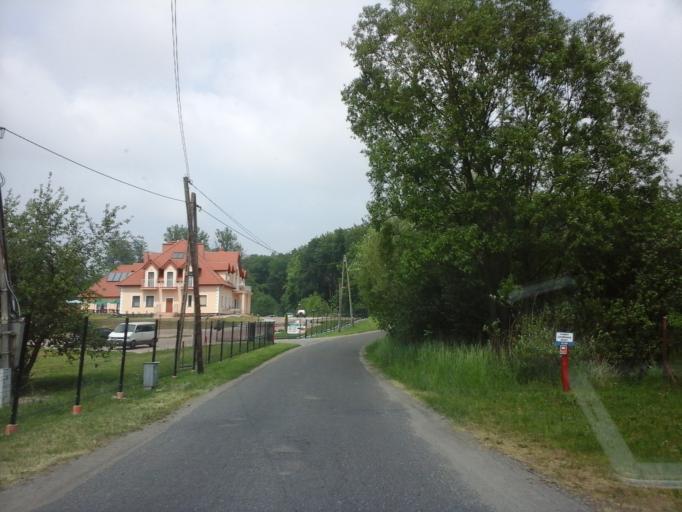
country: PL
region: West Pomeranian Voivodeship
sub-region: Powiat mysliborski
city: Barlinek
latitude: 53.0097
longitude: 15.2246
